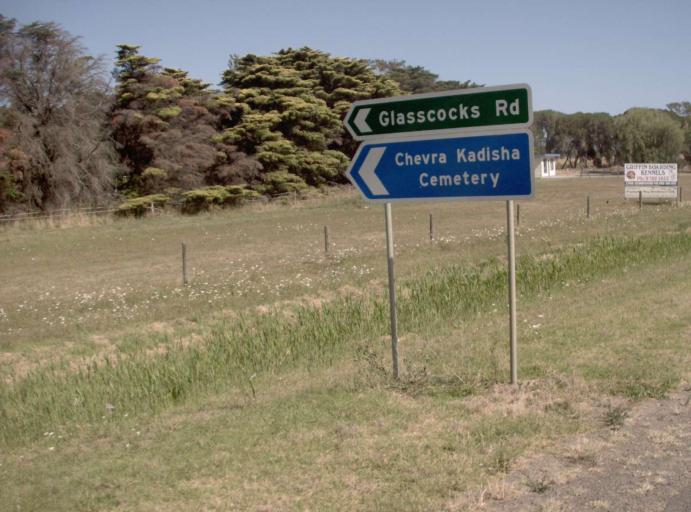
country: AU
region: Victoria
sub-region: Frankston
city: Sandhurst
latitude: -38.0571
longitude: 145.2069
